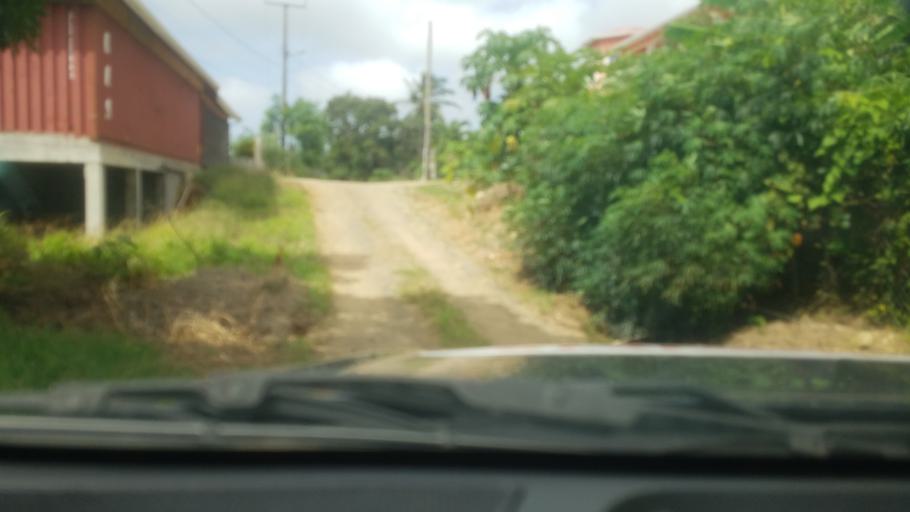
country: LC
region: Micoud Quarter
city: Micoud
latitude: 13.7961
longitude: -60.9301
